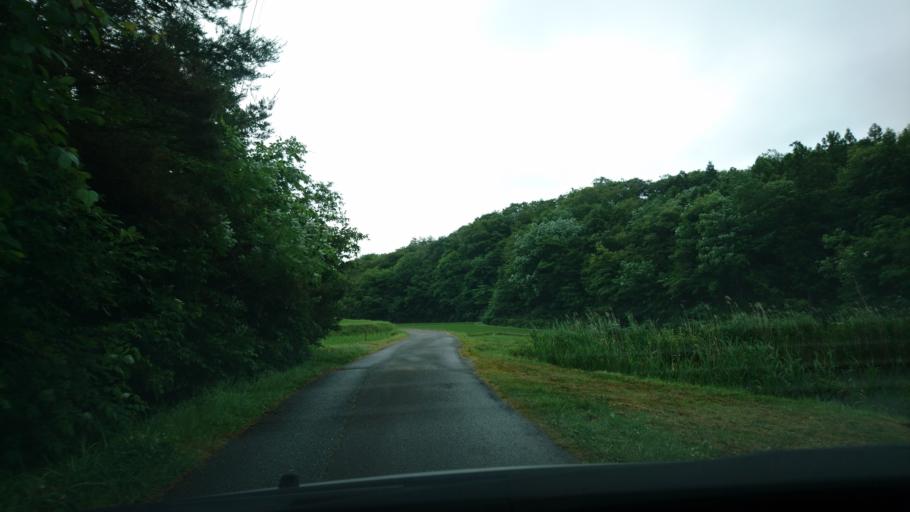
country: JP
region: Iwate
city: Ichinoseki
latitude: 38.8976
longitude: 141.1451
